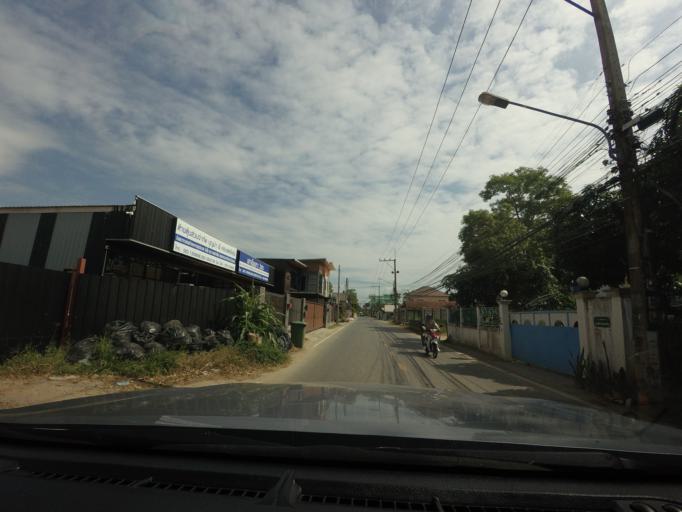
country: TH
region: Phitsanulok
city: Phitsanulok
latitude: 16.7972
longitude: 100.2490
